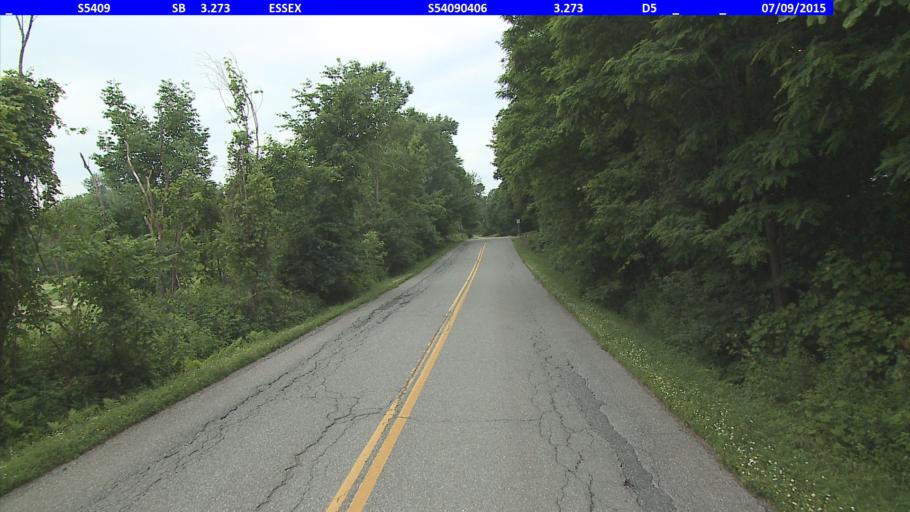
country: US
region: Vermont
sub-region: Chittenden County
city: Essex Junction
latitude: 44.5552
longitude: -73.0677
